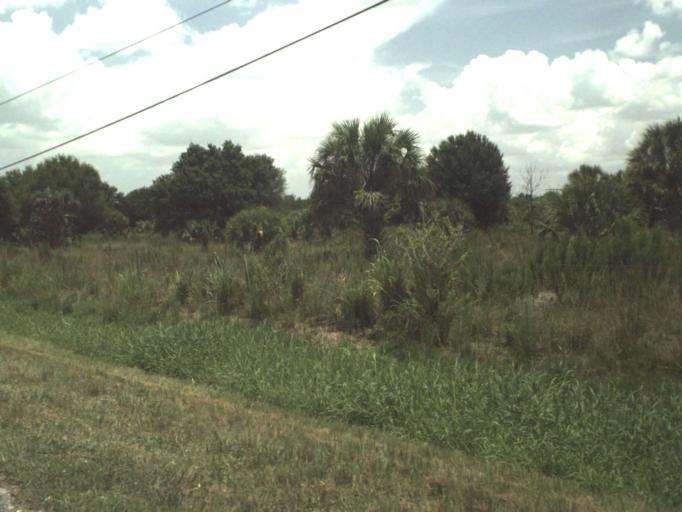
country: US
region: Florida
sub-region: Saint Lucie County
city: Fort Pierce South
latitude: 27.3745
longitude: -80.4643
